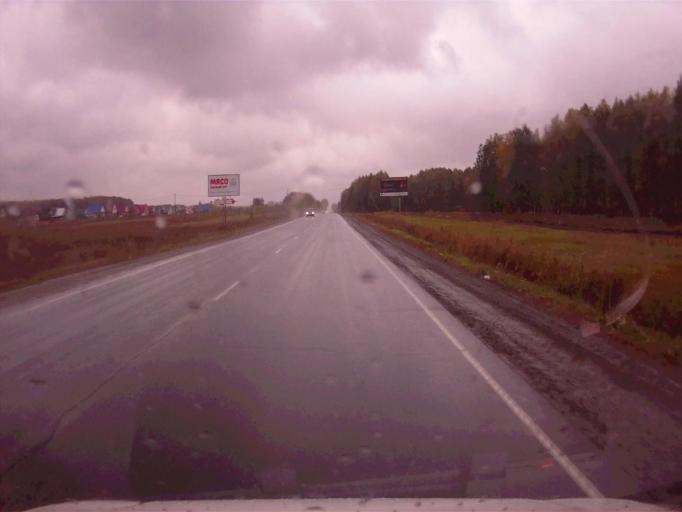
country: RU
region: Chelyabinsk
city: Argayash
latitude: 55.4202
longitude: 61.0178
